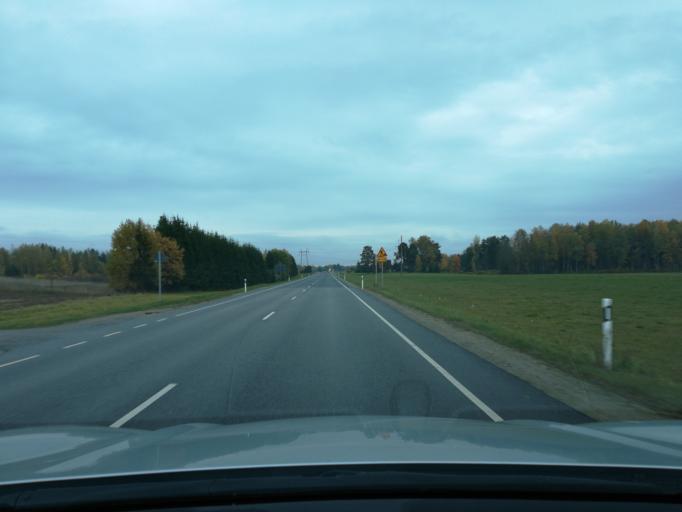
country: EE
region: Ida-Virumaa
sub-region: Johvi vald
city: Johvi
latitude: 59.0801
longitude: 27.3158
